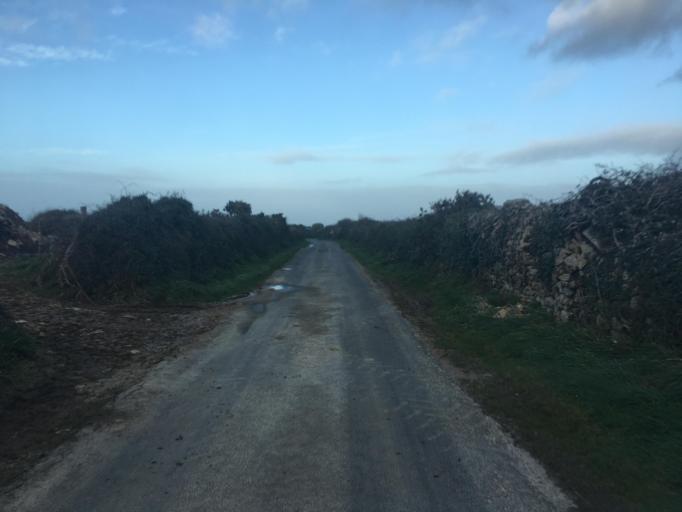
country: FR
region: Lower Normandy
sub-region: Departement de la Manche
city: Beaumont-Hague
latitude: 49.7161
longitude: -1.9213
